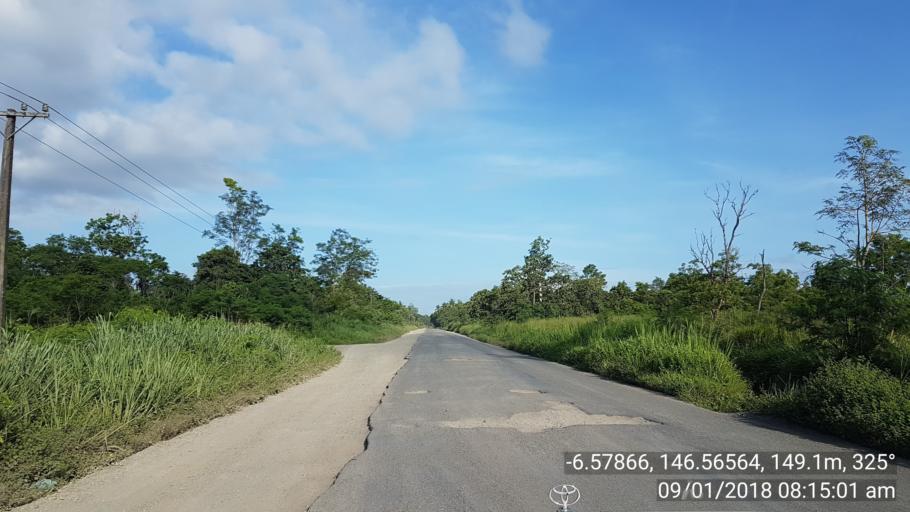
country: PG
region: Morobe
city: Lae
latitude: -6.5786
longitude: 146.5656
